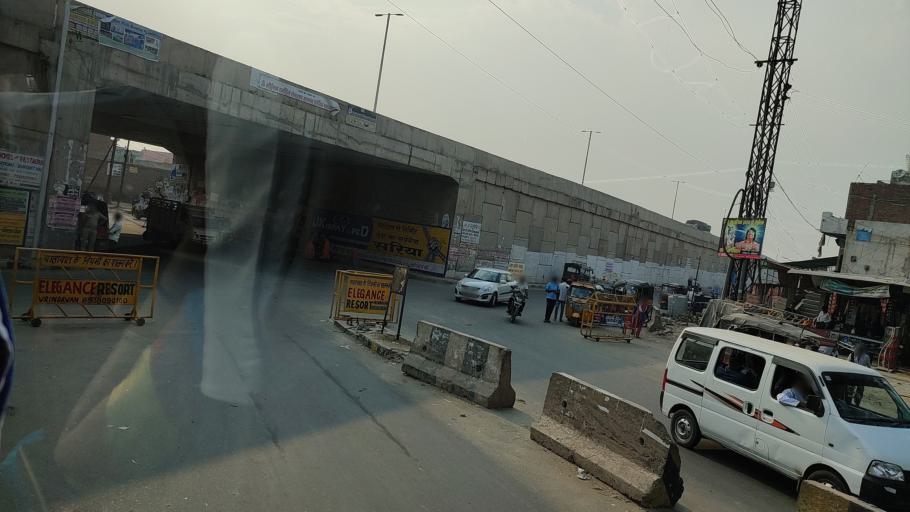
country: IN
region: Uttar Pradesh
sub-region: Mathura
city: Vrindavan
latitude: 27.5608
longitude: 77.6278
